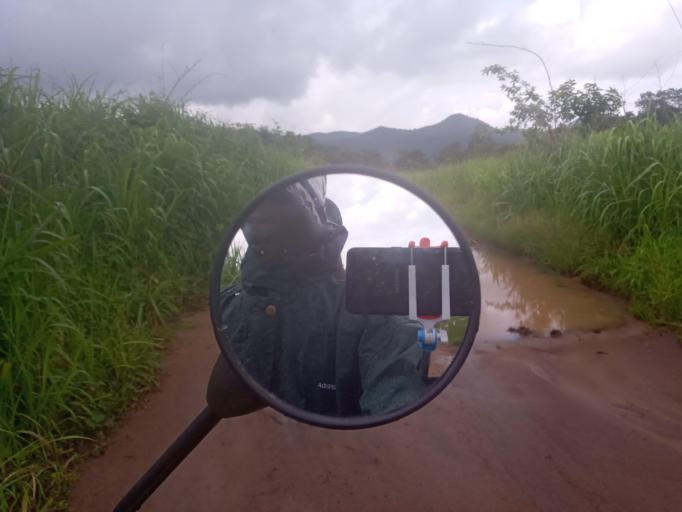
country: SL
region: Northern Province
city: Bumbuna
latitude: 8.9258
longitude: -11.7434
